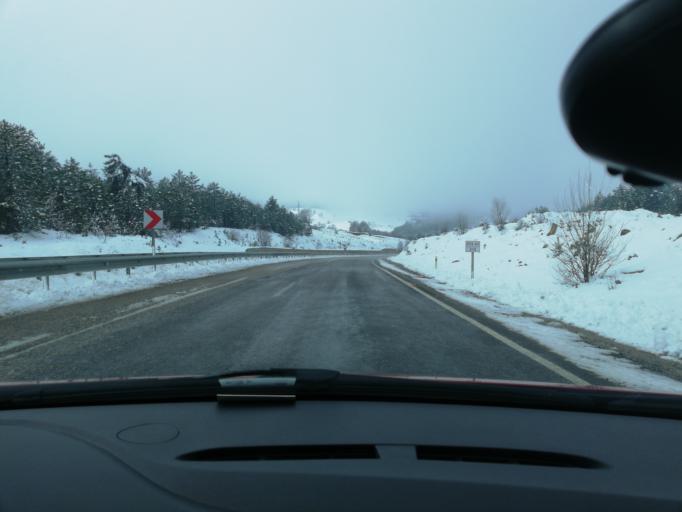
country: TR
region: Kastamonu
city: Akkaya
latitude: 41.2838
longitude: 33.4691
